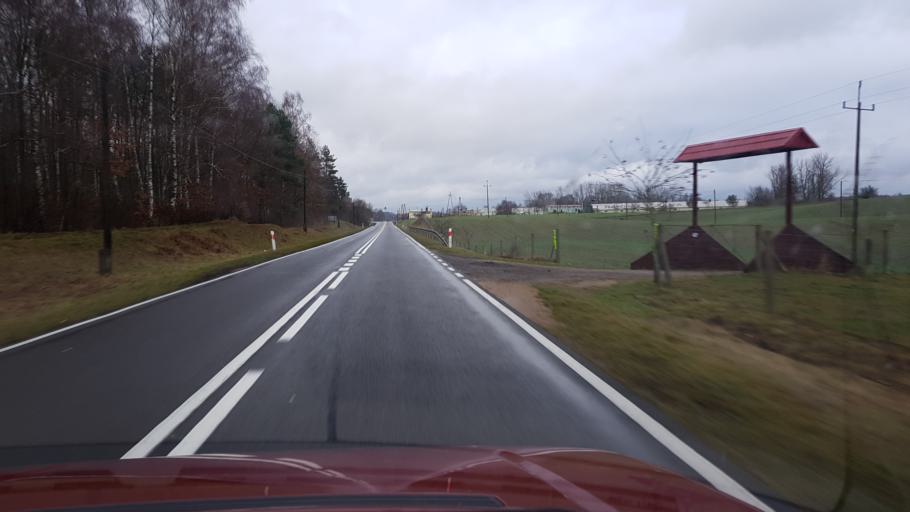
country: PL
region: West Pomeranian Voivodeship
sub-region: Powiat lobeski
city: Wegorzyno
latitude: 53.5175
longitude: 15.6367
